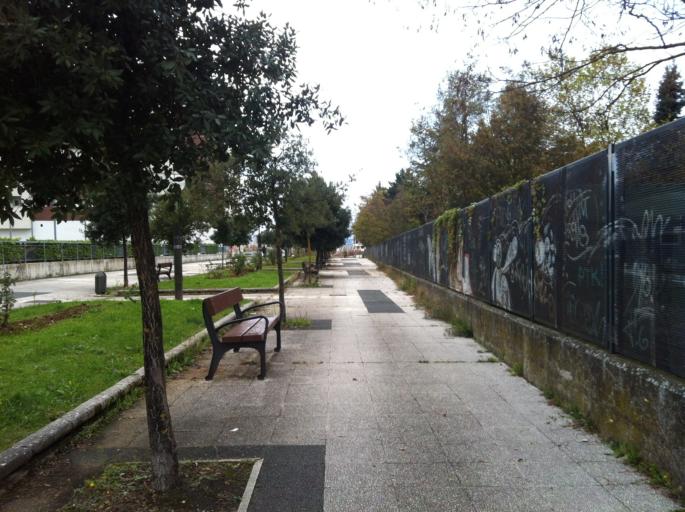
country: ES
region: Basque Country
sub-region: Provincia de Alava
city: Gasteiz / Vitoria
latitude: 42.8484
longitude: -2.6920
